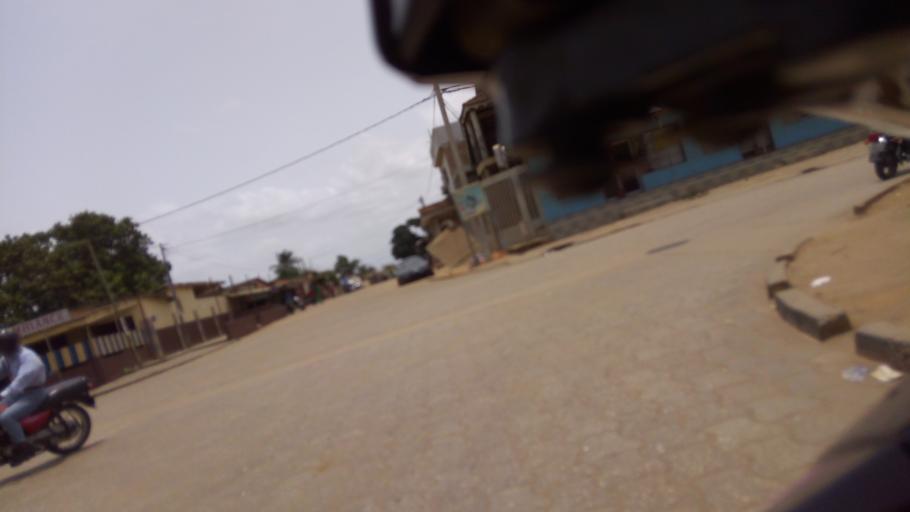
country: TG
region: Maritime
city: Lome
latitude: 6.1565
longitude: 1.2157
